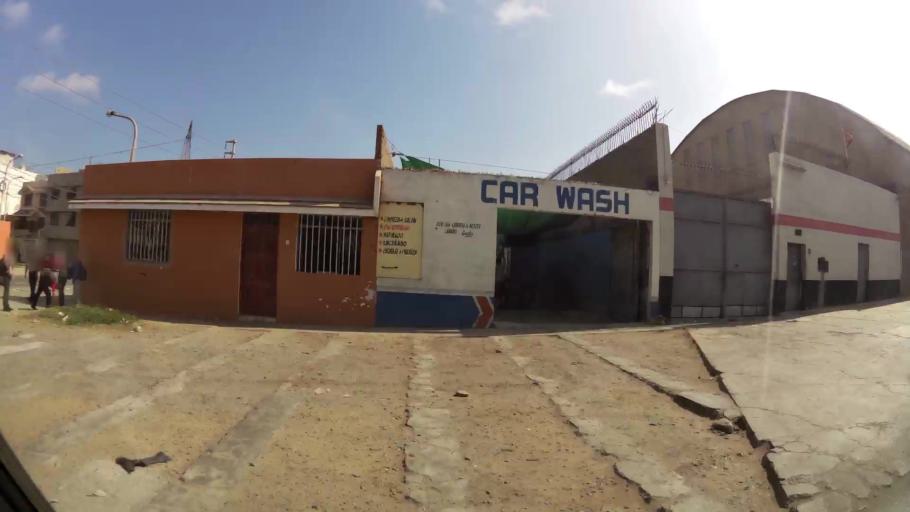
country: PE
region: La Libertad
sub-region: Provincia de Trujillo
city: Trujillo
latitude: -8.1260
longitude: -79.0202
